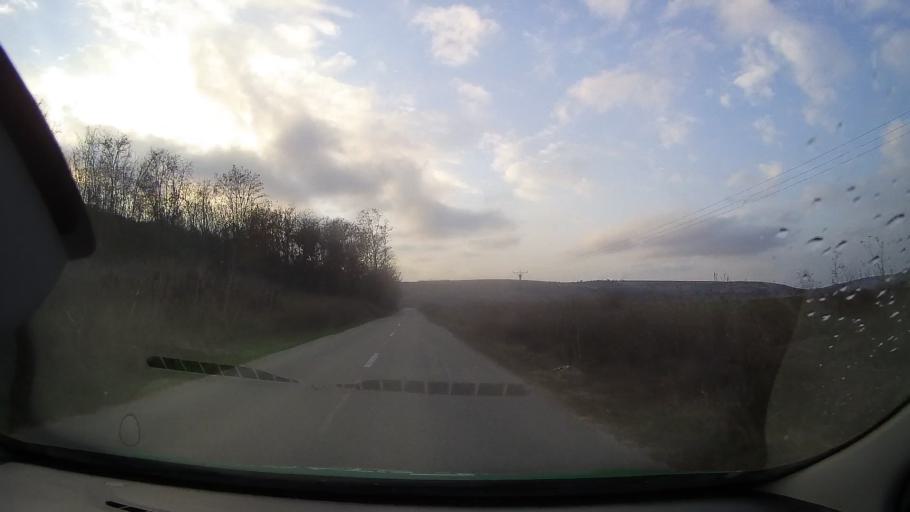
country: RO
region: Constanta
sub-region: Comuna Dobromir
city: Dobromir
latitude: 44.0352
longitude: 27.8490
